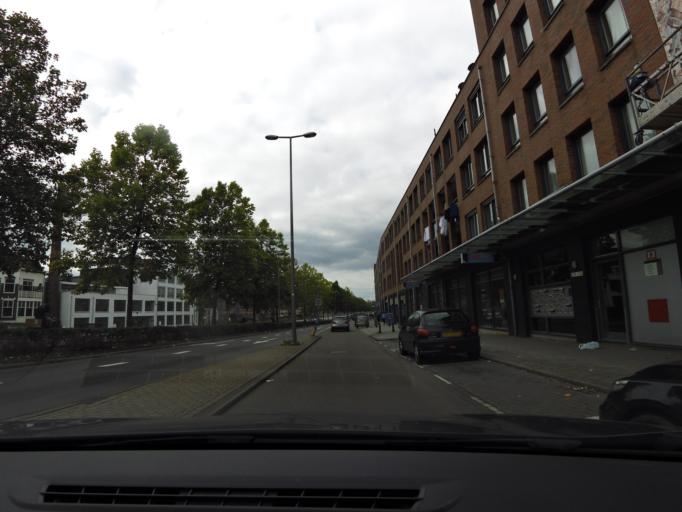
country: NL
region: South Holland
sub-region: Gemeente Rotterdam
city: Delfshaven
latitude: 51.9100
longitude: 4.4499
